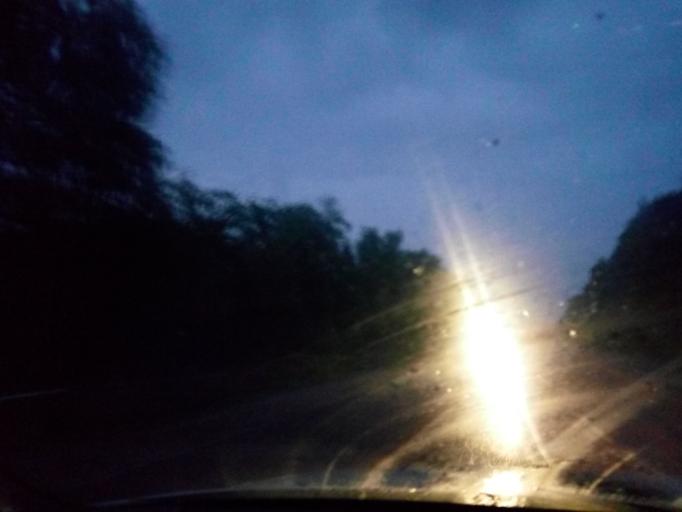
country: RU
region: Primorskiy
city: Dal'nerechensk
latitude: 45.8926
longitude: 133.7348
